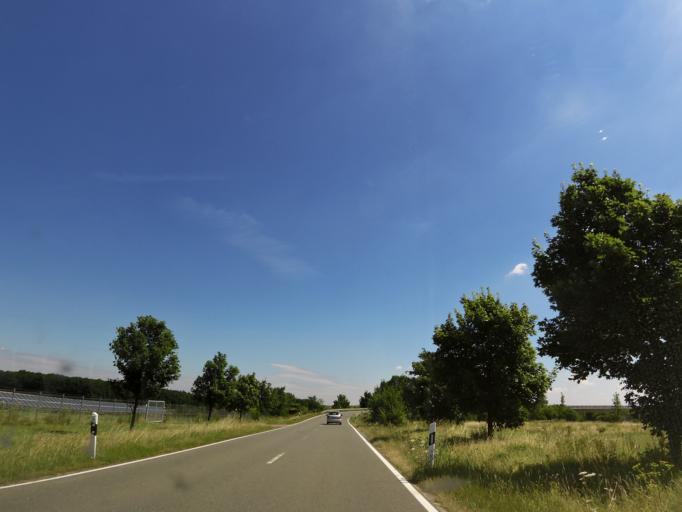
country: DE
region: Thuringia
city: Hartmannsdorf
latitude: 50.8979
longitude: 11.9757
